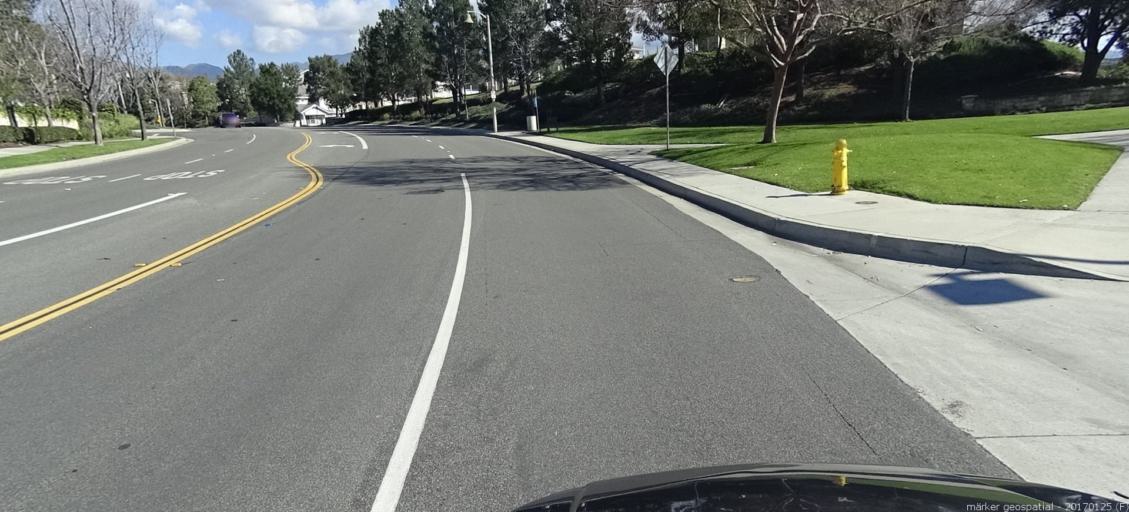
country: US
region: California
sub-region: Orange County
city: Foothill Ranch
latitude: 33.6799
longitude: -117.6526
